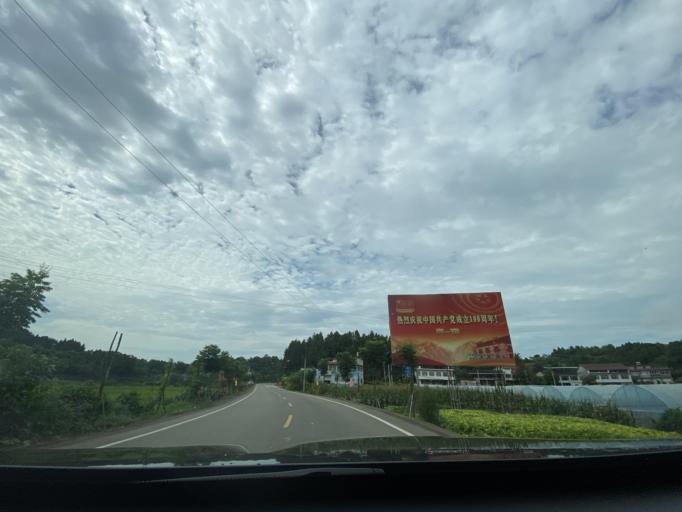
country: CN
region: Sichuan
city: Jiancheng
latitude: 30.4740
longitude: 104.6302
